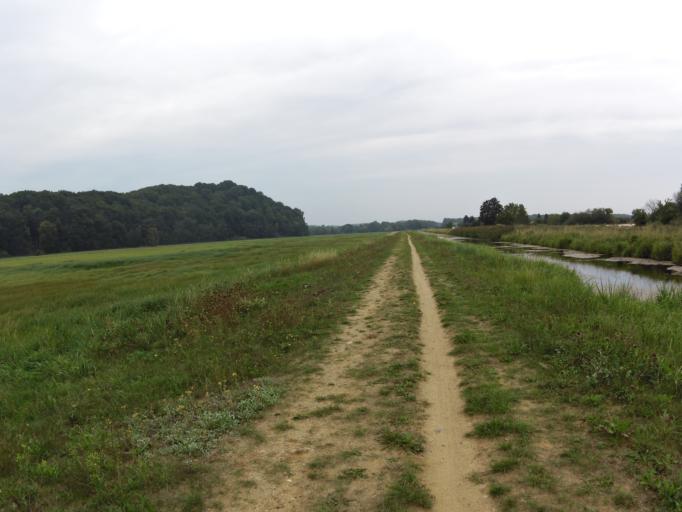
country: PL
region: West Pomeranian Voivodeship
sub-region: Swinoujscie
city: Swinoujscie
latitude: 53.8814
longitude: 14.2150
